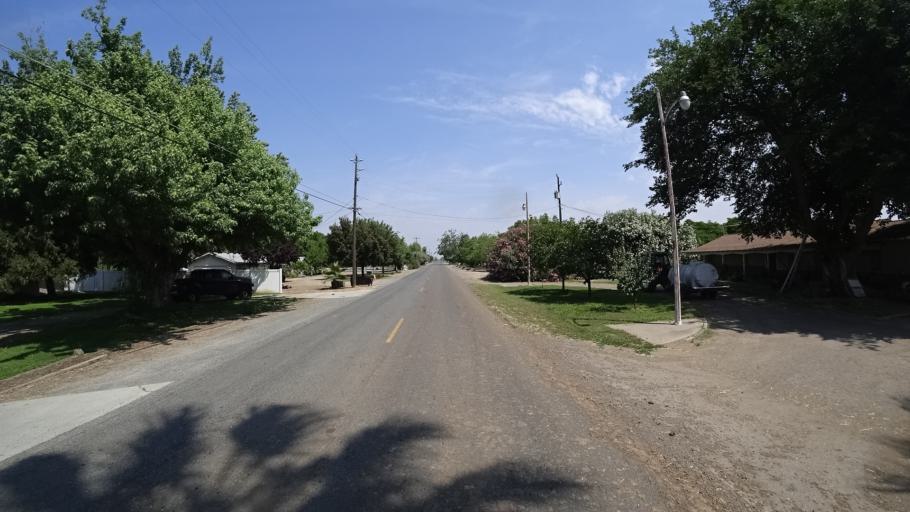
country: US
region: California
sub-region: Kings County
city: Lemoore
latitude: 36.3173
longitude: -119.7628
